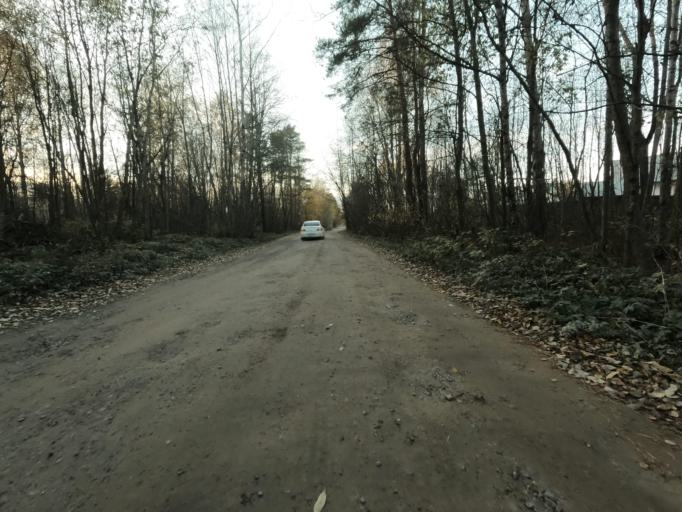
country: RU
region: Leningrad
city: Mga
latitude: 59.7609
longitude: 31.2603
